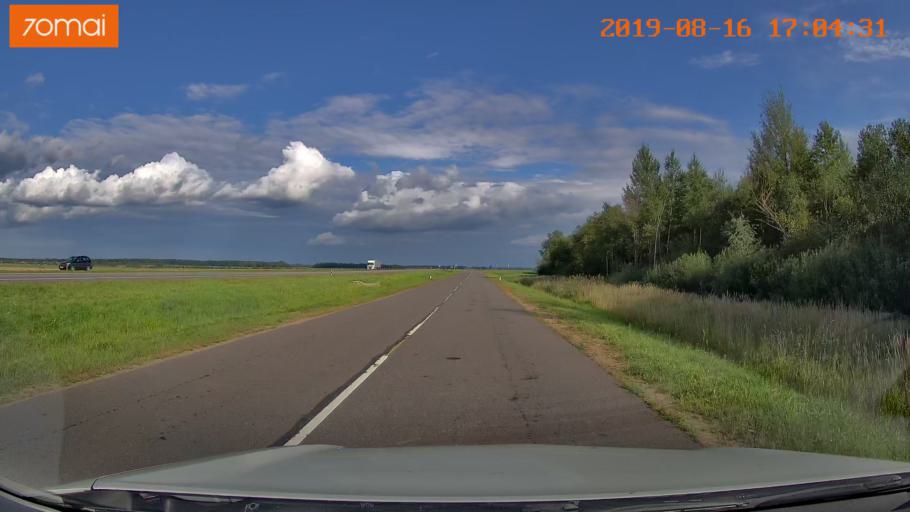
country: BY
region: Mogilev
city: Yalizava
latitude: 53.2430
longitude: 28.9469
